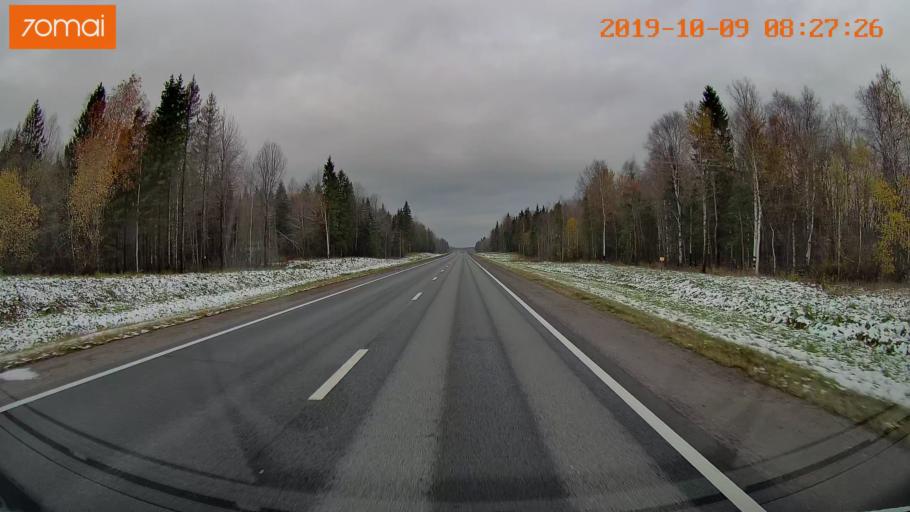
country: RU
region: Vologda
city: Gryazovets
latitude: 58.8039
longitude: 40.2485
